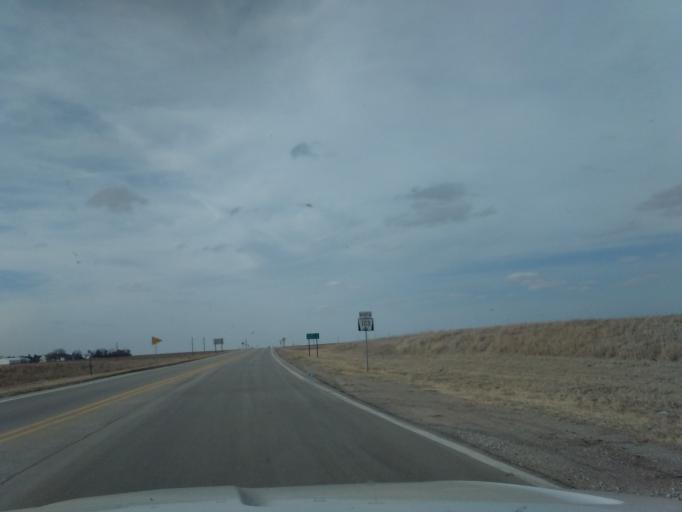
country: US
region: Nebraska
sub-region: Gage County
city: Beatrice
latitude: 40.3071
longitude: -96.9139
